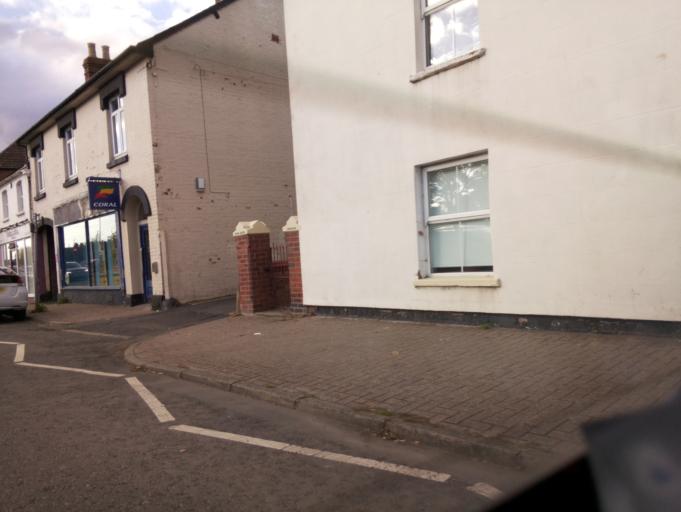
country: GB
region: England
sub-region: Herefordshire
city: Hereford
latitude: 52.0571
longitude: -2.7230
